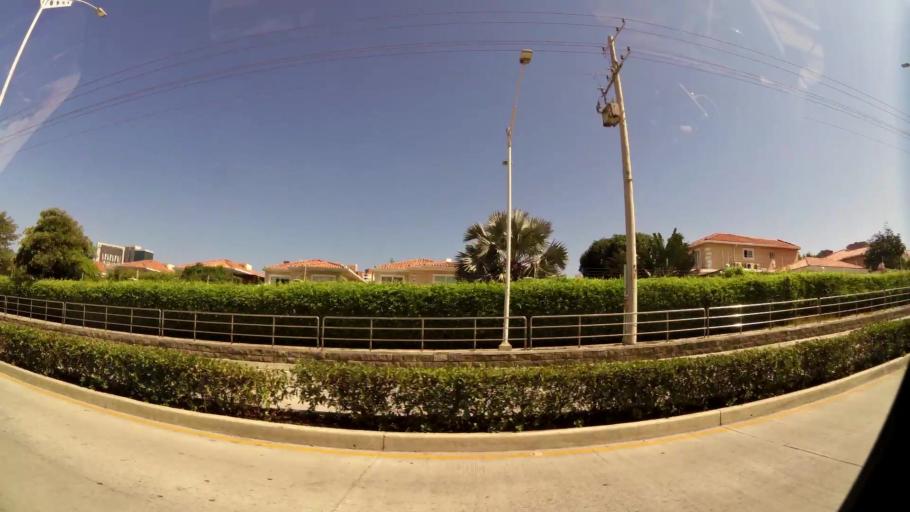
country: CO
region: Atlantico
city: Barranquilla
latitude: 11.0137
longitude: -74.8350
